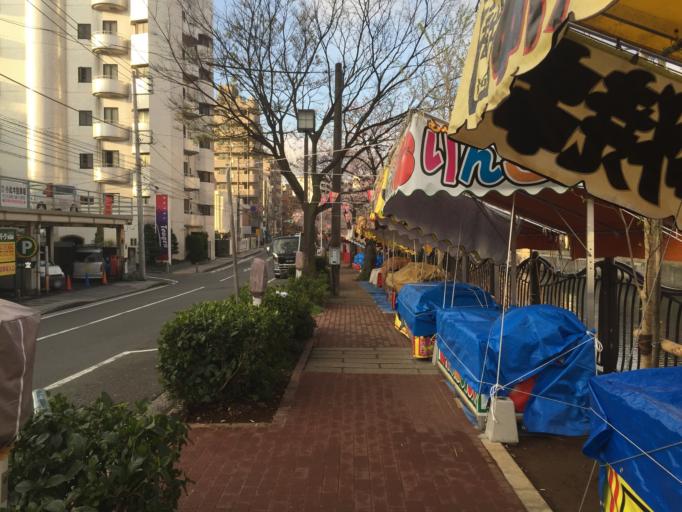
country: JP
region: Kanagawa
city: Yokohama
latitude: 35.4434
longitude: 139.6271
